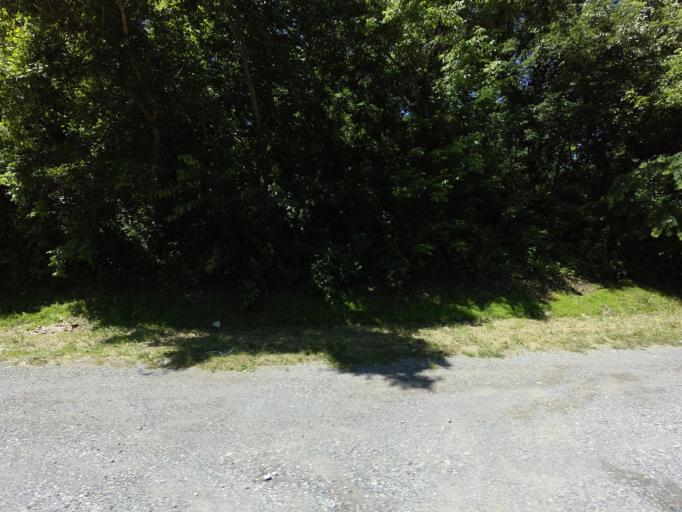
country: US
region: Maryland
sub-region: Frederick County
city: Brunswick
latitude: 39.3350
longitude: -77.6852
